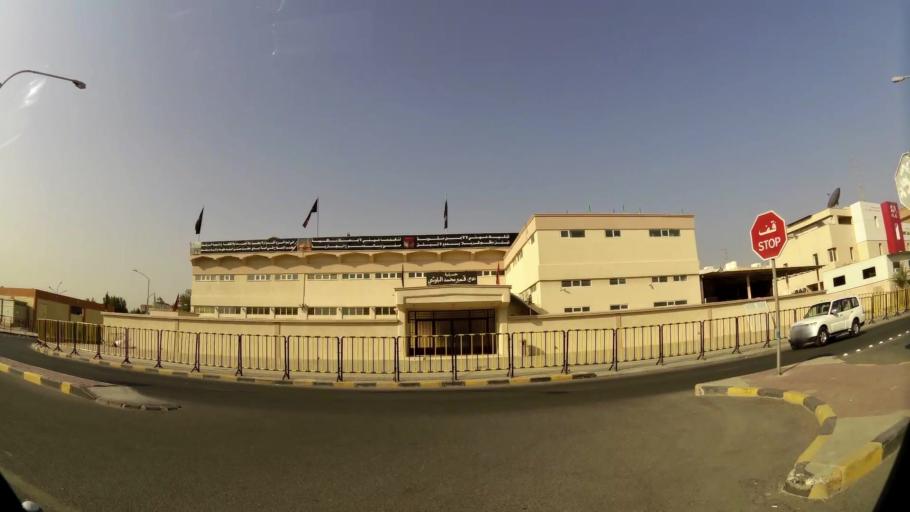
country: KW
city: Bayan
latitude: 29.3176
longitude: 48.0438
